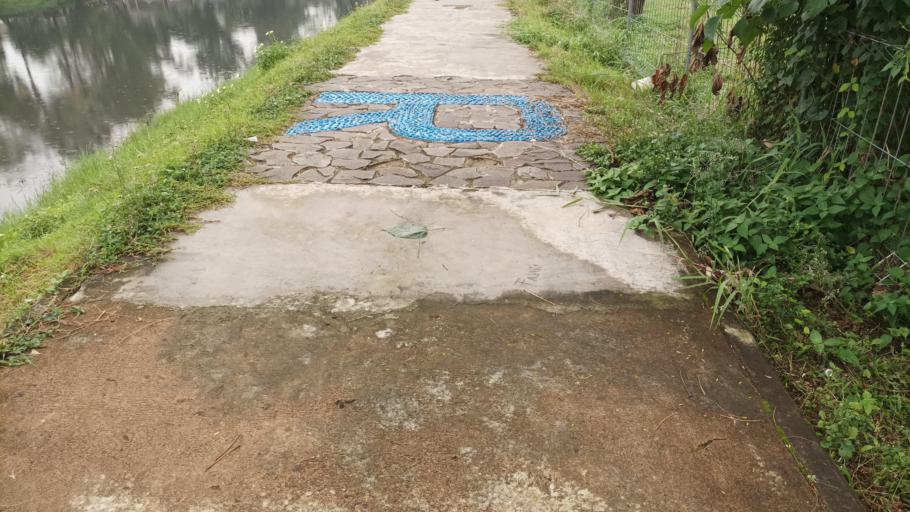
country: ID
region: West Java
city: Cileungsir
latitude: -6.3904
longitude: 106.9153
